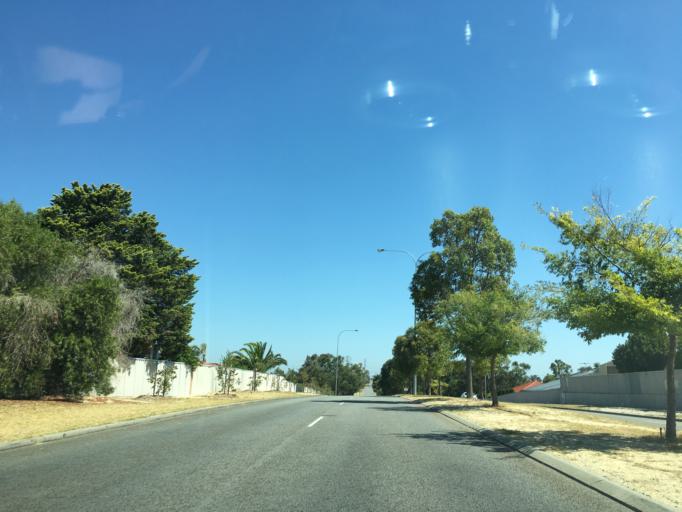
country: AU
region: Western Australia
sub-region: Canning
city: Canning Vale
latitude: -32.0501
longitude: 115.9043
